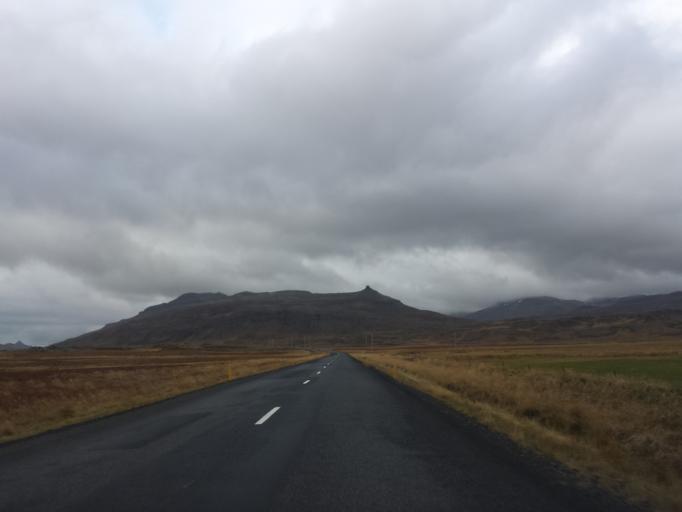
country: IS
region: West
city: Stykkisholmur
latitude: 64.8625
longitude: -22.7533
